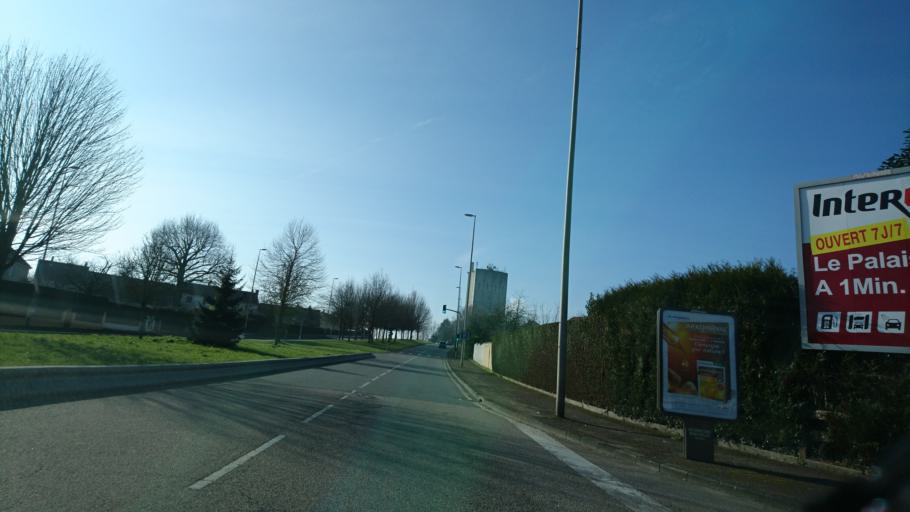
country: FR
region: Limousin
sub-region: Departement de la Haute-Vienne
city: Le Palais-sur-Vienne
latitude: 45.8753
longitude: 1.3007
